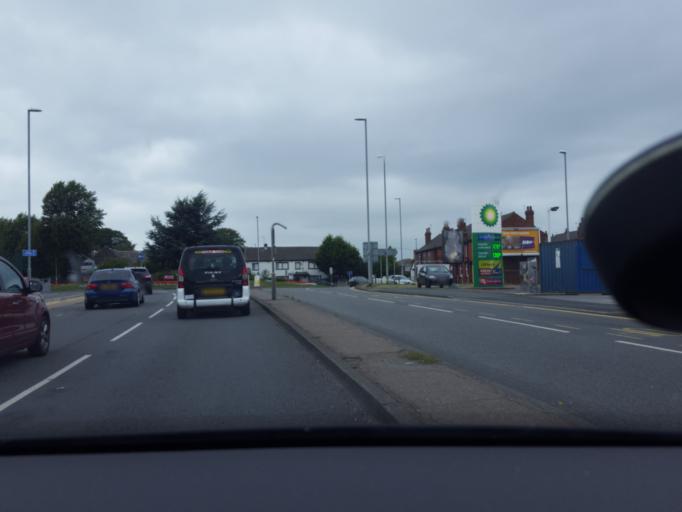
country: GB
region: England
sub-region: City and Borough of Leeds
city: Horsforth
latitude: 53.8048
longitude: -1.6216
